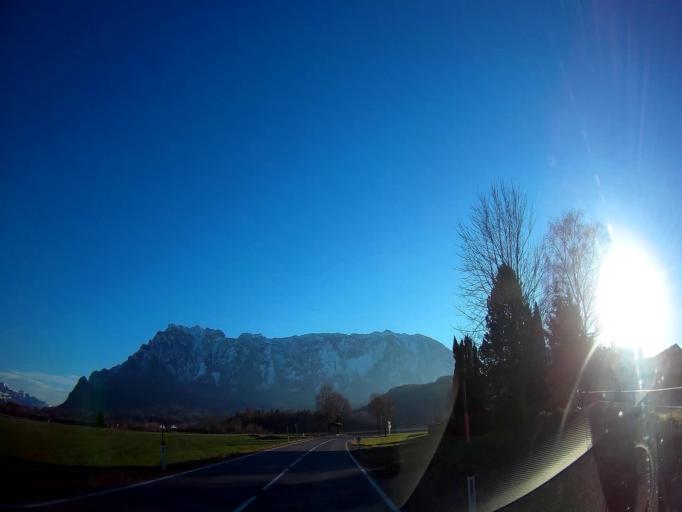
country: DE
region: Bavaria
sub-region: Upper Bavaria
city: Ainring
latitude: 47.7747
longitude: 12.9604
